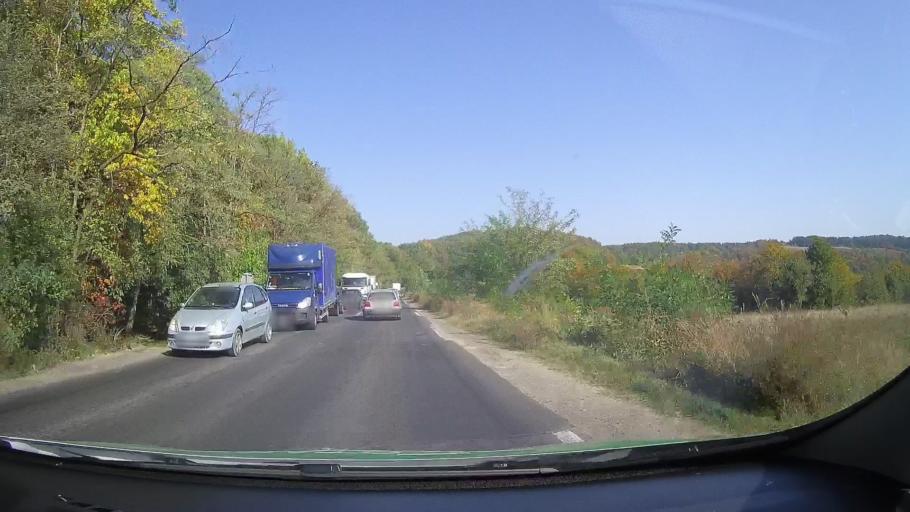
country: RO
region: Timis
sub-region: Comuna Curtea
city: Curtea
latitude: 45.8612
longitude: 22.3427
